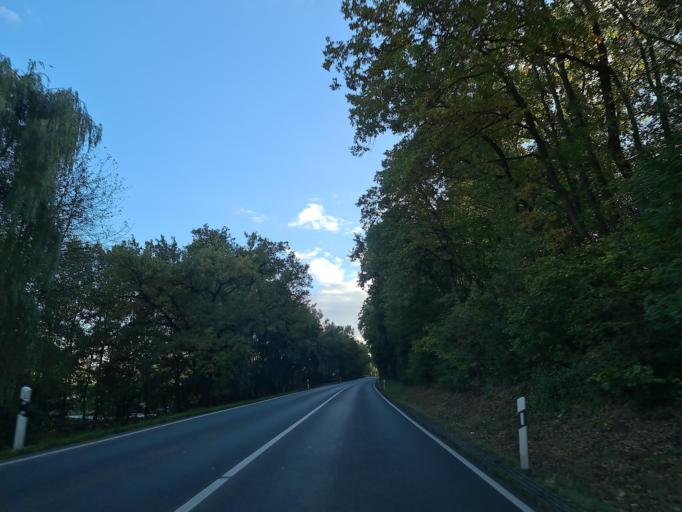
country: DE
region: Thuringia
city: Wunschendorf
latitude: 50.8197
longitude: 12.0772
